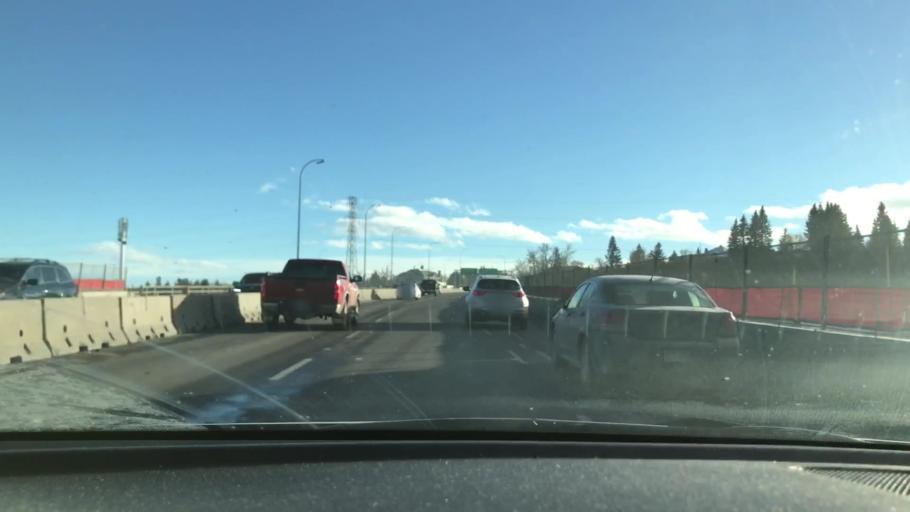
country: CA
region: Alberta
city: Calgary
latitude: 51.0475
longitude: -114.1153
